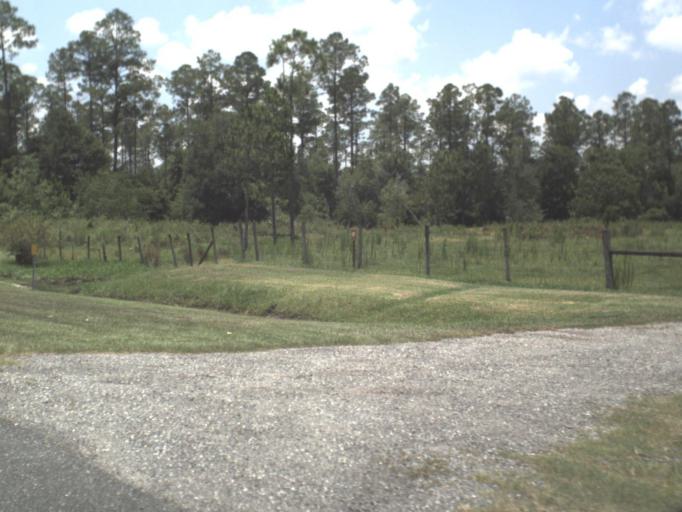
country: US
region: Florida
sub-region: Union County
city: Lake Butler
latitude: 30.0701
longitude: -82.2155
